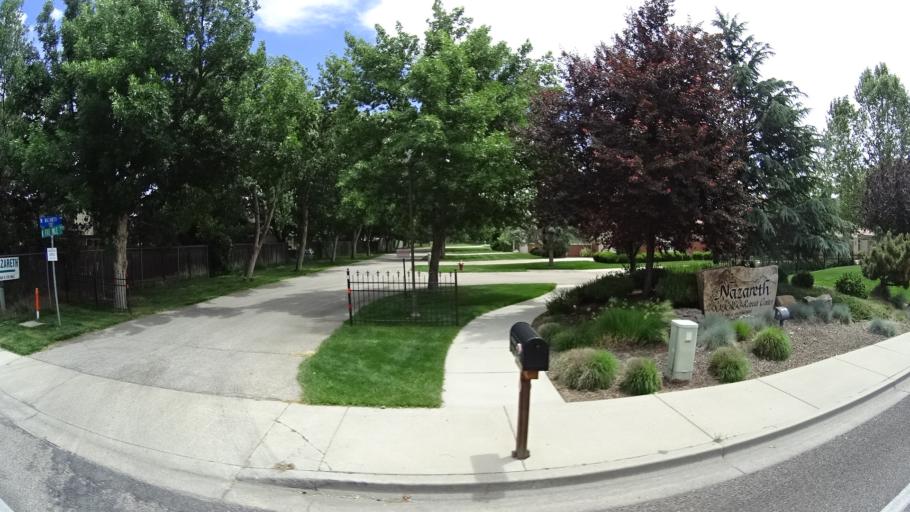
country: US
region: Idaho
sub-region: Ada County
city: Eagle
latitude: 43.6455
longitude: -116.3142
